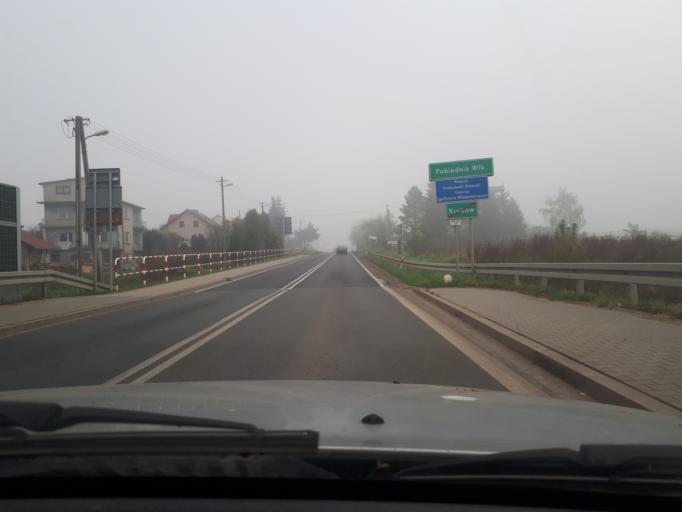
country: PL
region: Lesser Poland Voivodeship
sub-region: Powiat wielicki
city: Niepolomice
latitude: 50.0811
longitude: 20.1912
